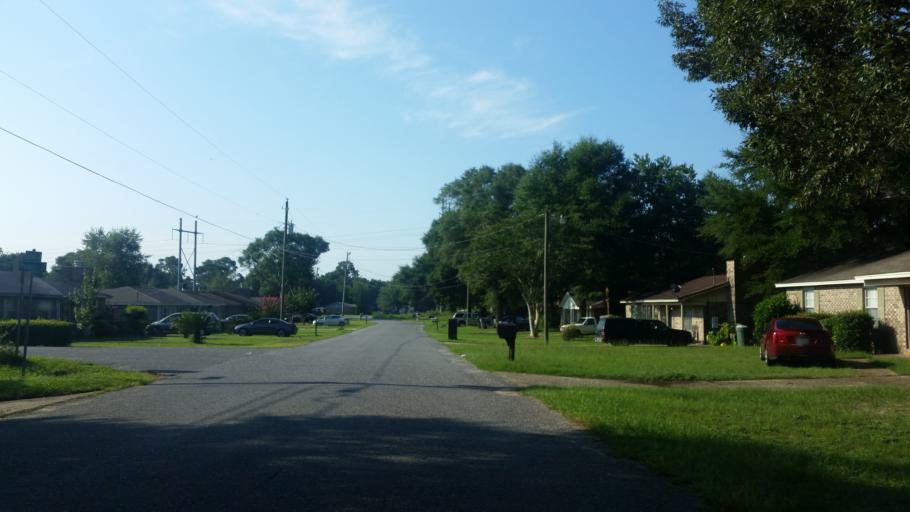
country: US
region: Florida
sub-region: Escambia County
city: Bellview
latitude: 30.4721
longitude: -87.2942
